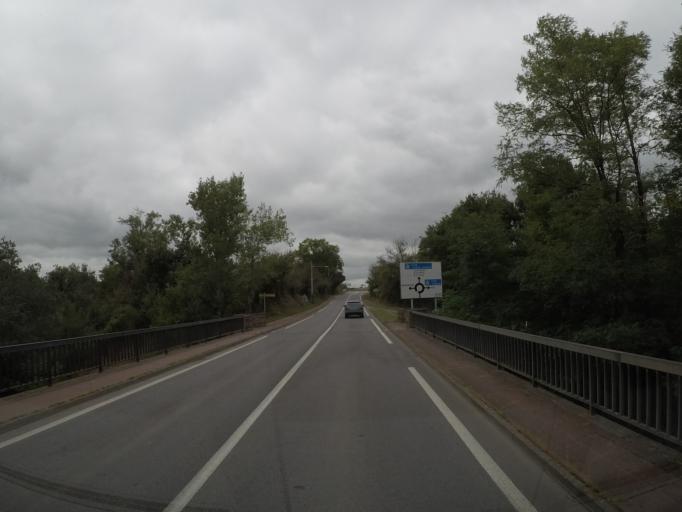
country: FR
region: Midi-Pyrenees
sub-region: Departement de la Haute-Garonne
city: Marquefave
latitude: 43.3390
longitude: 1.2585
